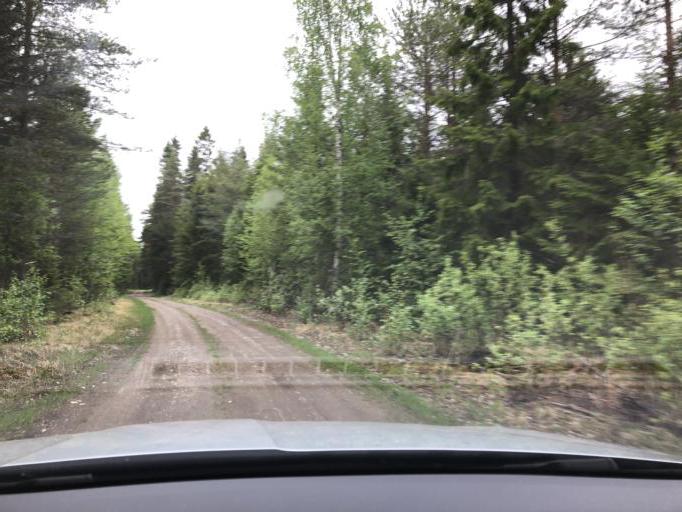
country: SE
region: Norrbotten
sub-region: Pitea Kommun
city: Roknas
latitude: 65.3932
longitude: 21.2688
